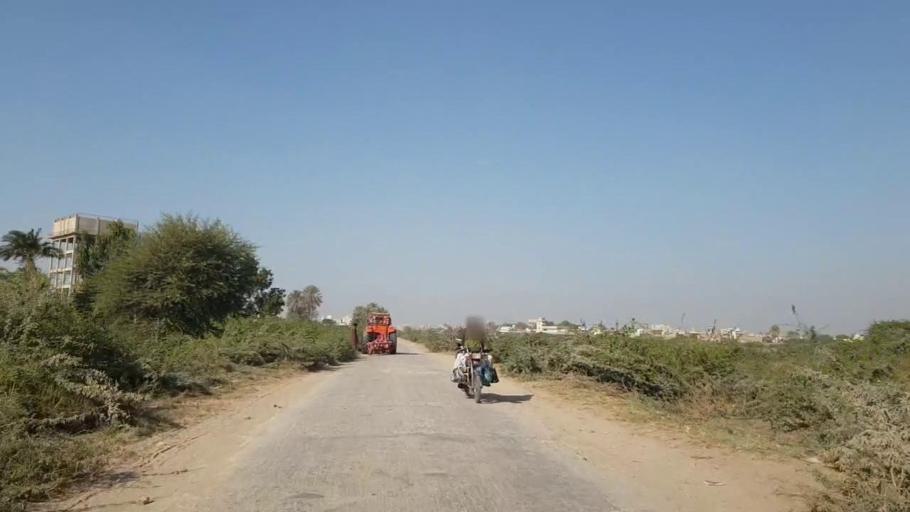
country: PK
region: Sindh
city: Digri
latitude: 25.1440
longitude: 69.1117
